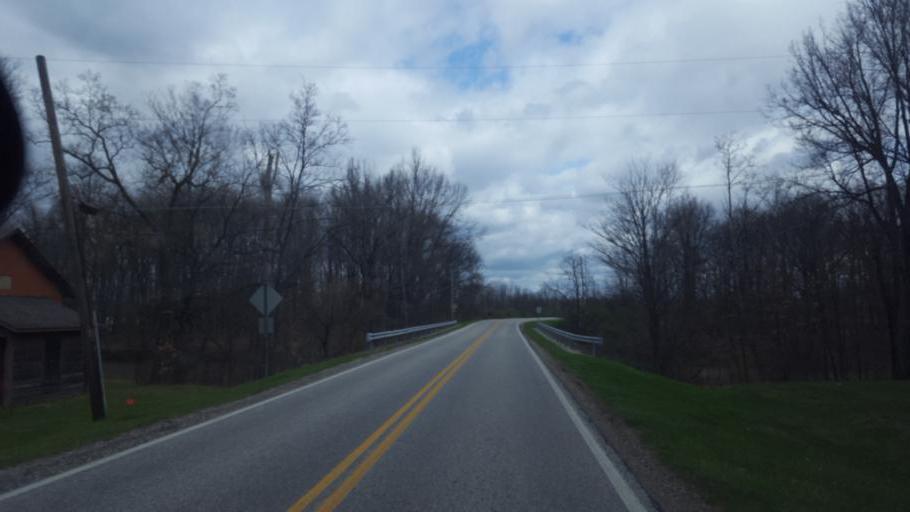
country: US
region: Ohio
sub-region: Franklin County
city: Westerville
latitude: 40.1534
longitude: -82.8708
